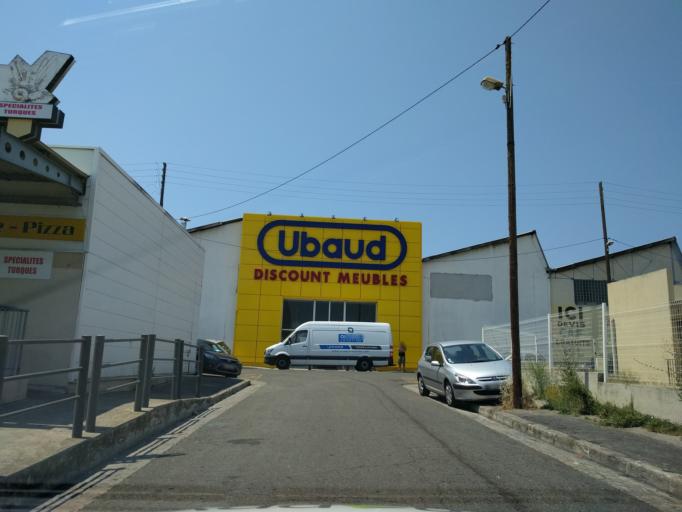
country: FR
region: Provence-Alpes-Cote d'Azur
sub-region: Departement des Bouches-du-Rhone
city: Marseille 14
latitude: 43.3413
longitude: 5.3596
